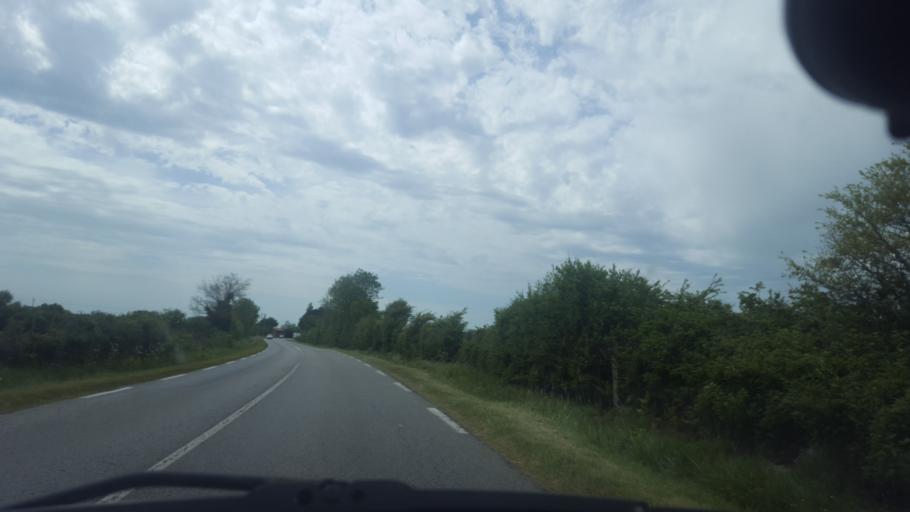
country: FR
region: Pays de la Loire
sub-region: Departement de la Loire-Atlantique
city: Saint-Meme-le-Tenu
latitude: 46.9917
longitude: -1.7811
